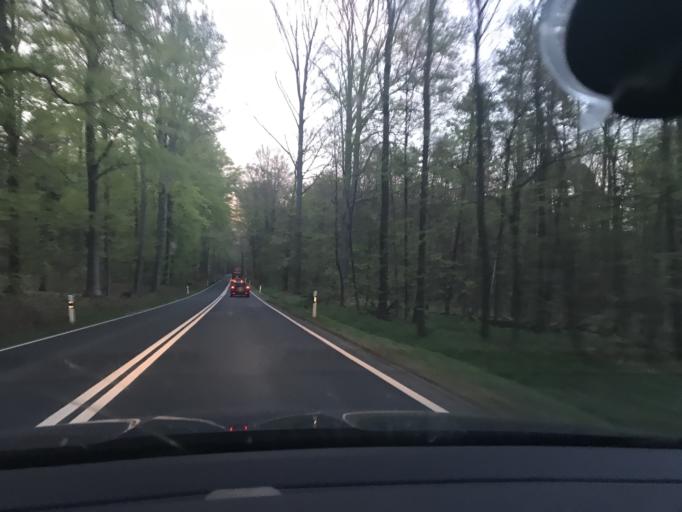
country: DE
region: Saxony
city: Ottendorf-Okrilla
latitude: 51.2162
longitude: 13.8413
